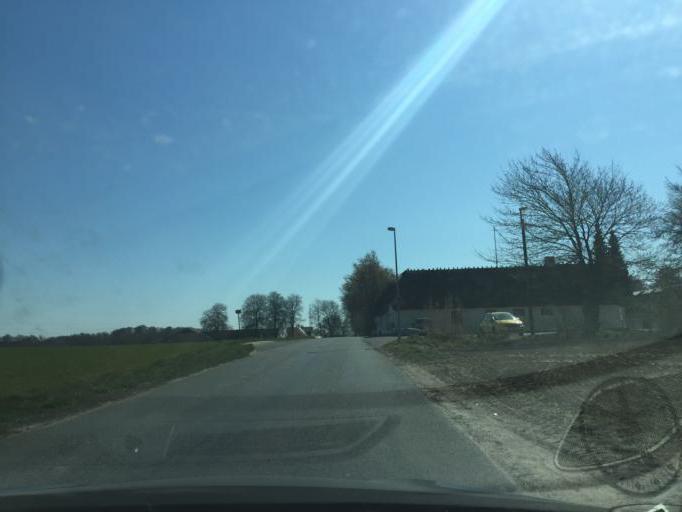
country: DK
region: South Denmark
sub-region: Faaborg-Midtfyn Kommune
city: Ringe
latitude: 55.2528
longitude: 10.5075
